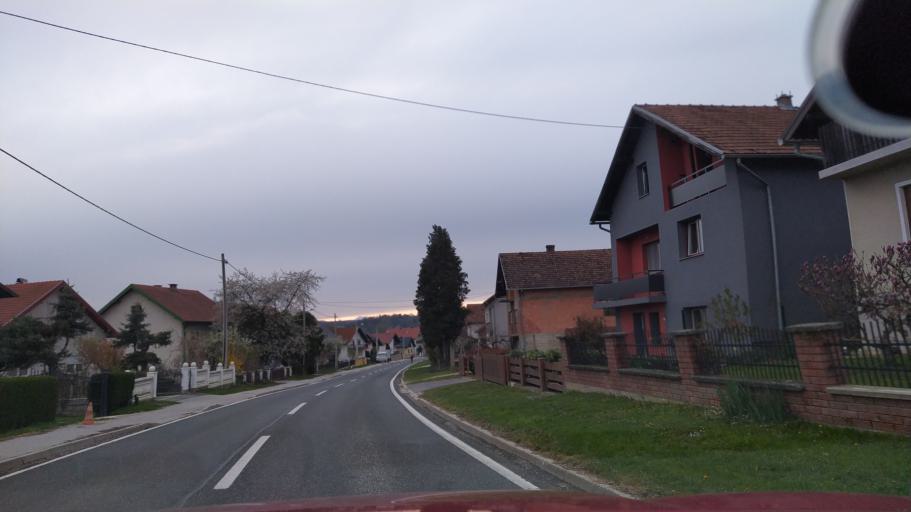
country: HR
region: Varazdinska
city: Jalzabet
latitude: 46.2089
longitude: 16.4465
